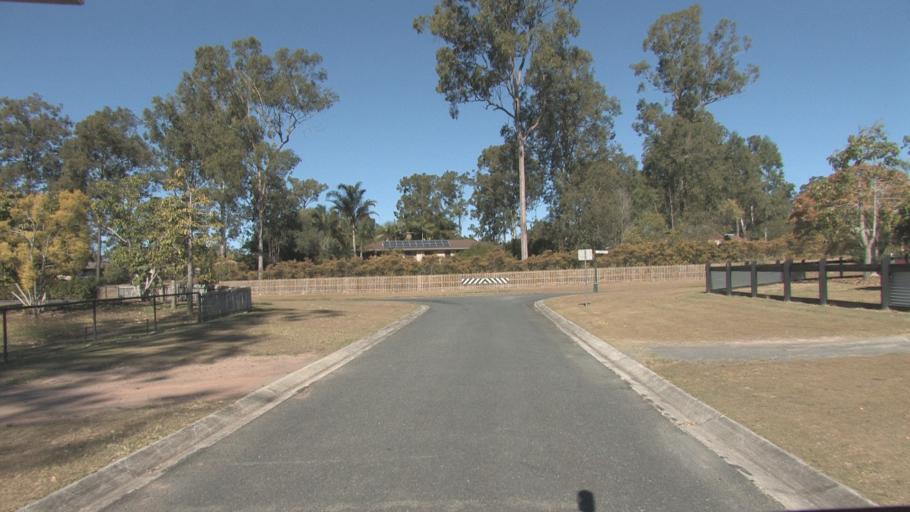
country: AU
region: Queensland
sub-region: Logan
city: North Maclean
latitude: -27.8176
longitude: 152.9466
